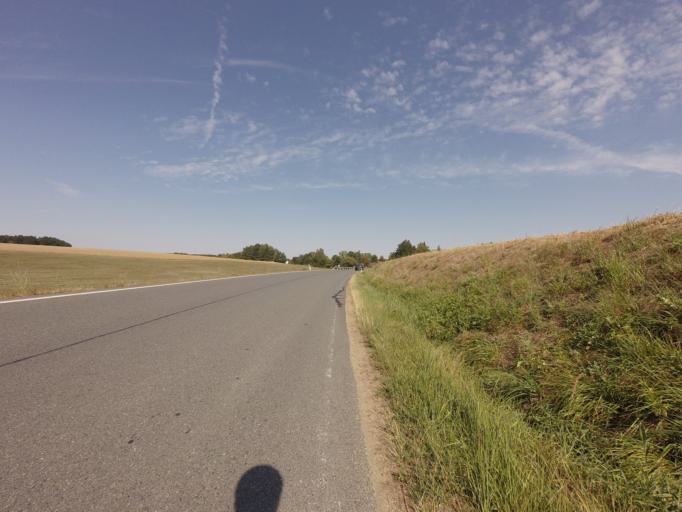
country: CZ
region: Jihocesky
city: Bernartice
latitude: 49.3785
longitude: 14.3690
